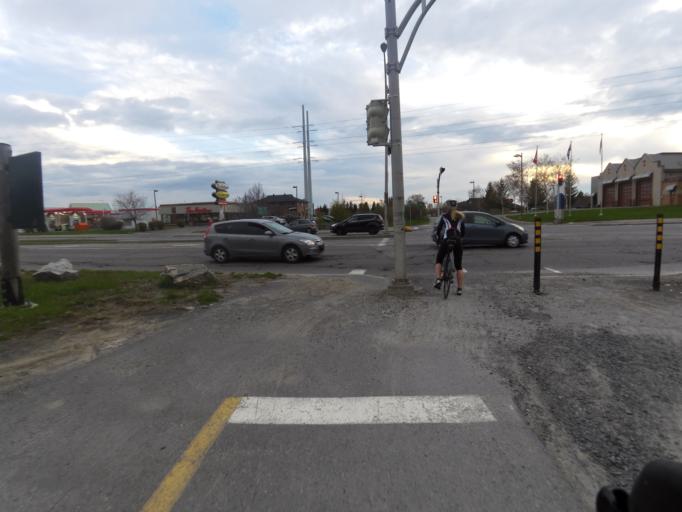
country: CA
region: Ontario
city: Ottawa
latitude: 45.4375
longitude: -75.7660
